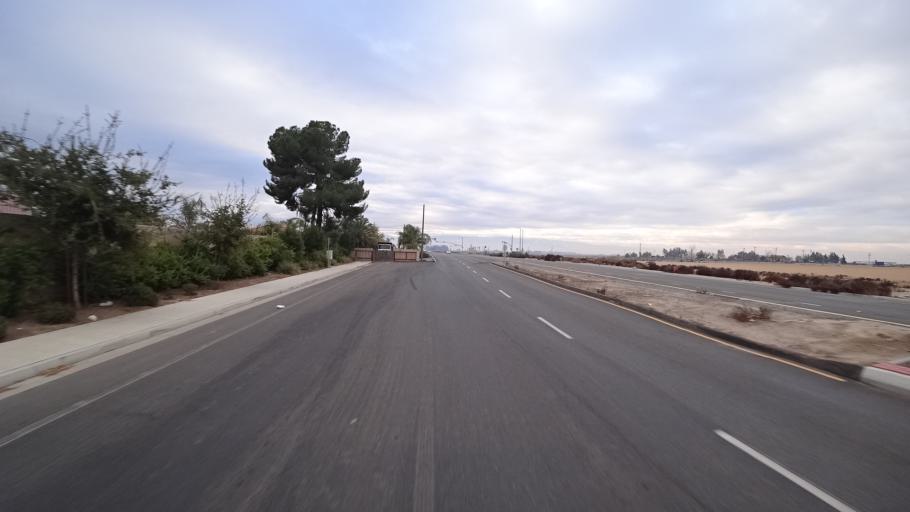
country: US
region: California
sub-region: Kern County
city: Greenfield
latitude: 35.2689
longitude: -119.0743
